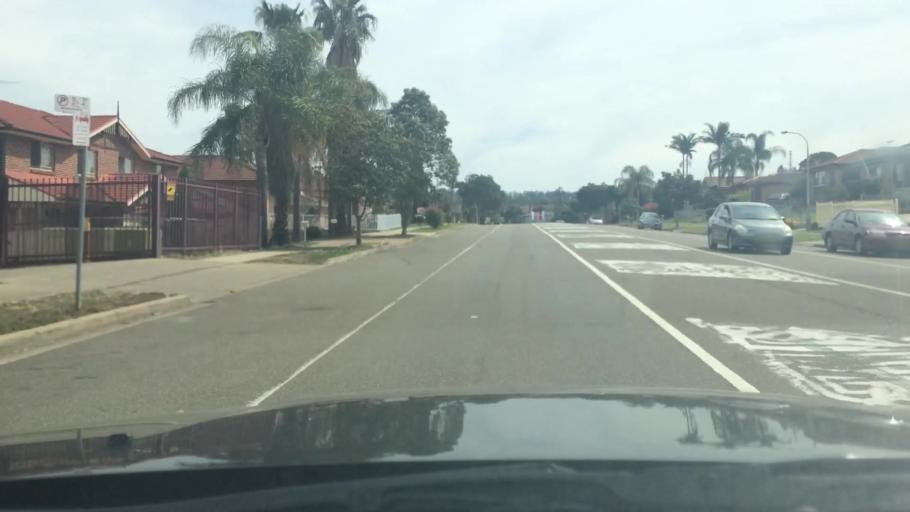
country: AU
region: New South Wales
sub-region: Fairfield
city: Cecil Park
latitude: -33.8696
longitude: 150.8743
